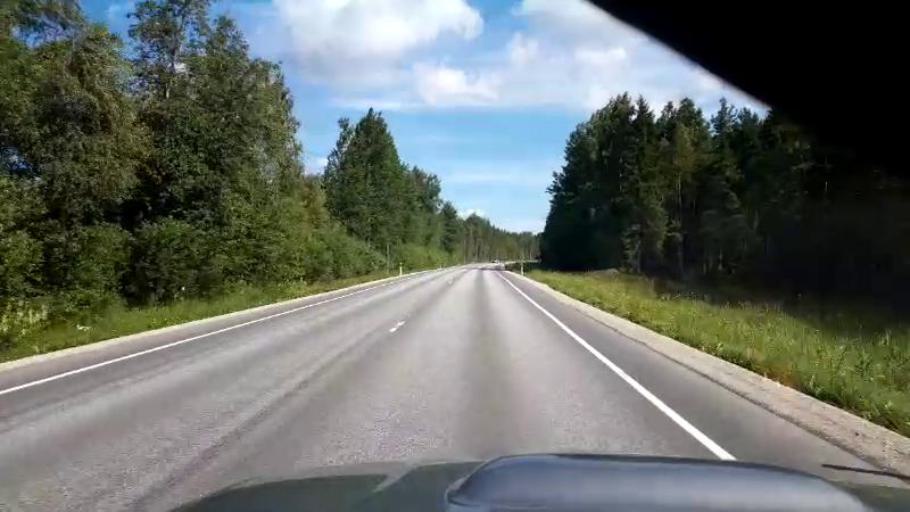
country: EE
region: Jaervamaa
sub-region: Paide linn
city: Paide
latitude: 58.9986
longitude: 25.6771
